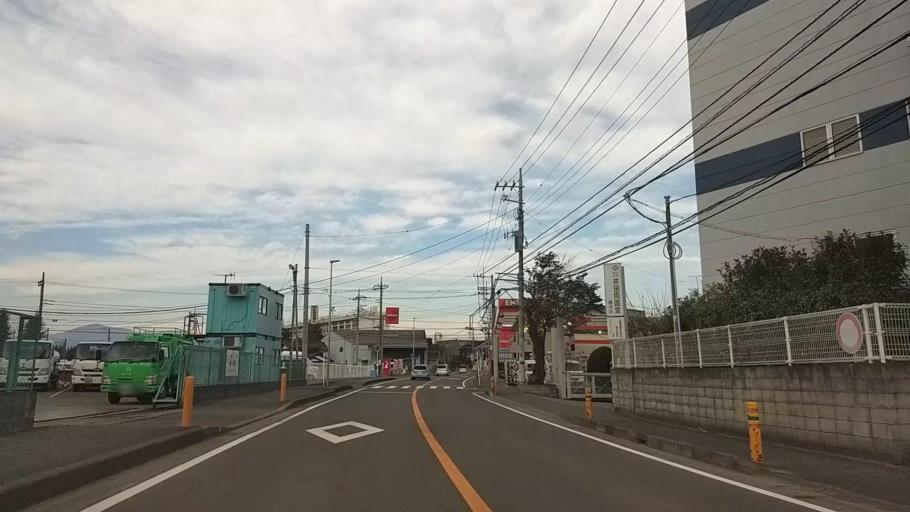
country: JP
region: Kanagawa
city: Atsugi
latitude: 35.4012
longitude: 139.4242
